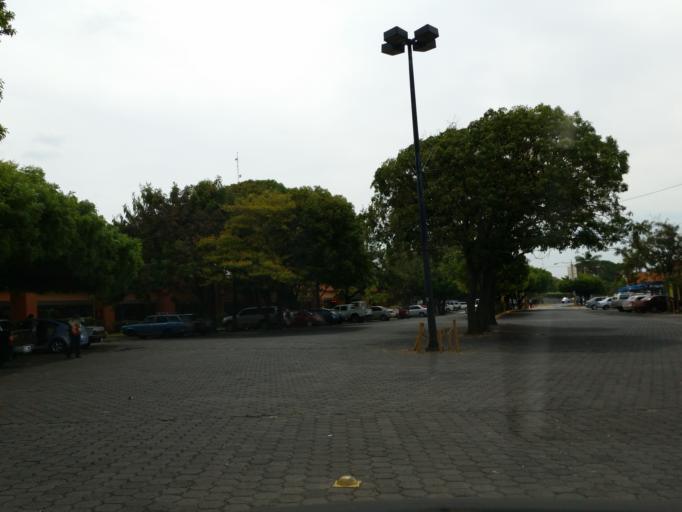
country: NI
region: Managua
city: Managua
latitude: 12.1157
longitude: -86.2476
